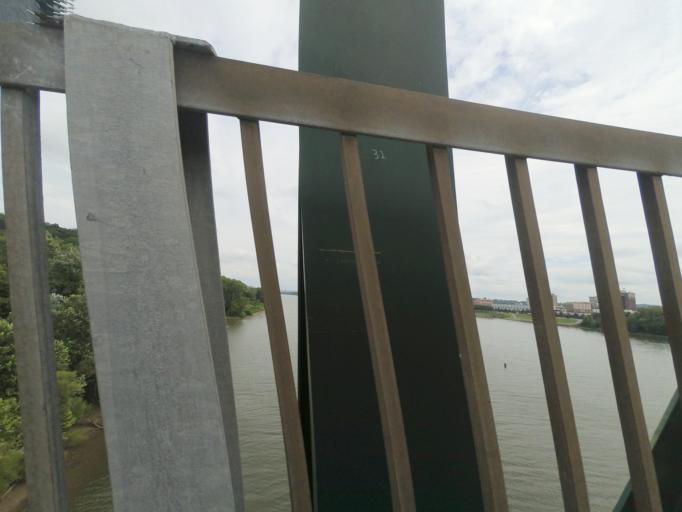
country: US
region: West Virginia
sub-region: Cabell County
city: Huntington
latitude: 38.4264
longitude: -82.4518
